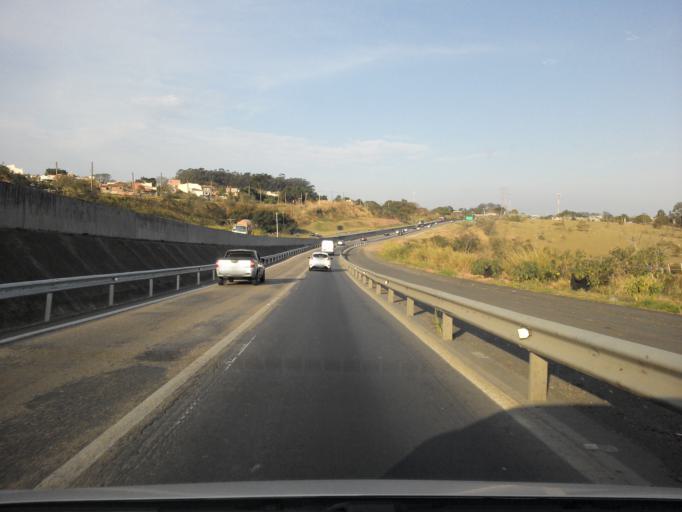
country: BR
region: Sao Paulo
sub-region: Hortolandia
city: Hortolandia
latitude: -22.8854
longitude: -47.1549
